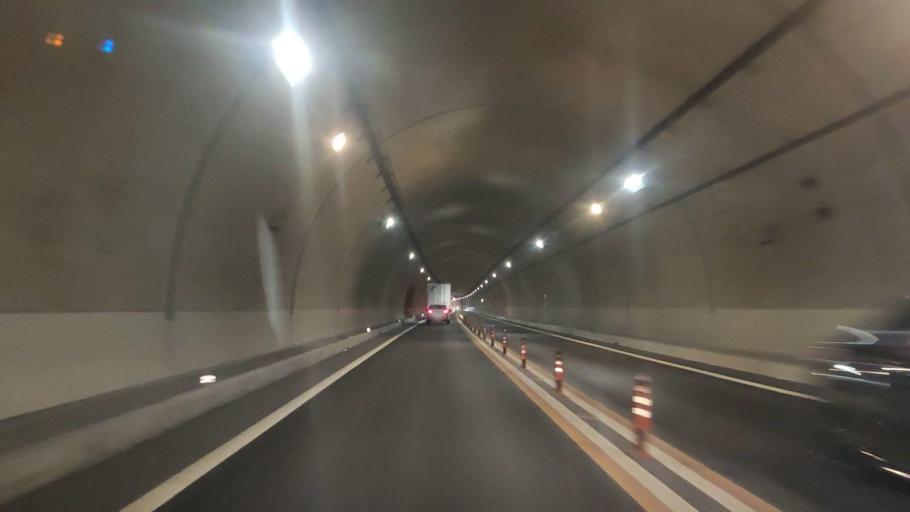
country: JP
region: Fukuoka
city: Kanda
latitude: 33.7725
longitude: 130.9680
